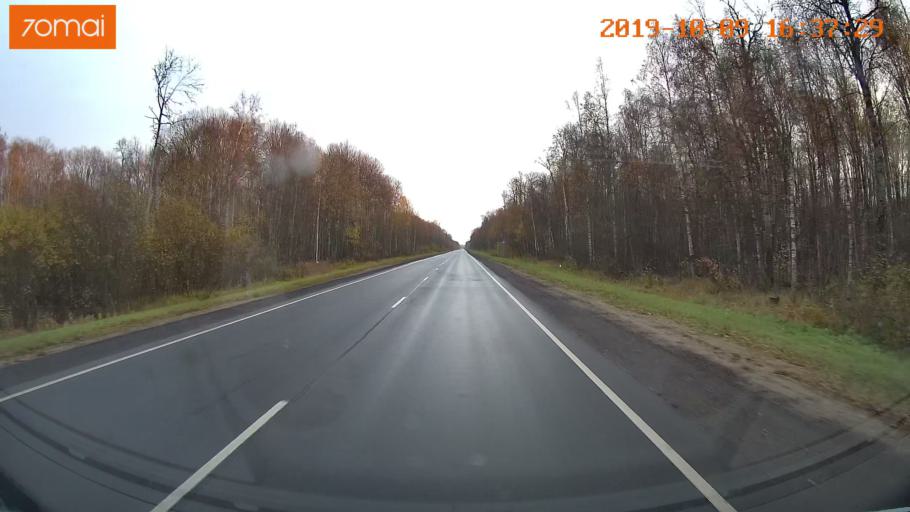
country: RU
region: Kostroma
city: Volgorechensk
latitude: 57.5263
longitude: 41.0252
